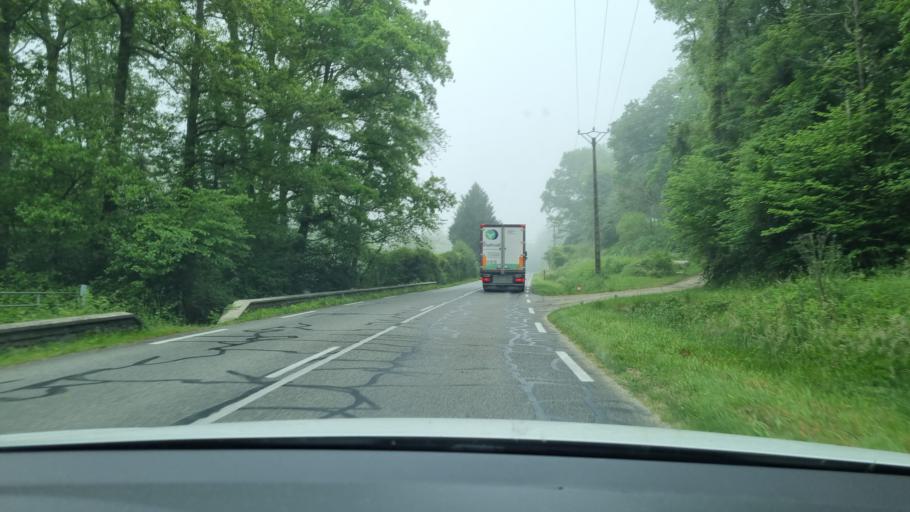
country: FR
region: Aquitaine
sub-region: Departement des Pyrenees-Atlantiques
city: Orthez
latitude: 43.5172
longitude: -0.7226
